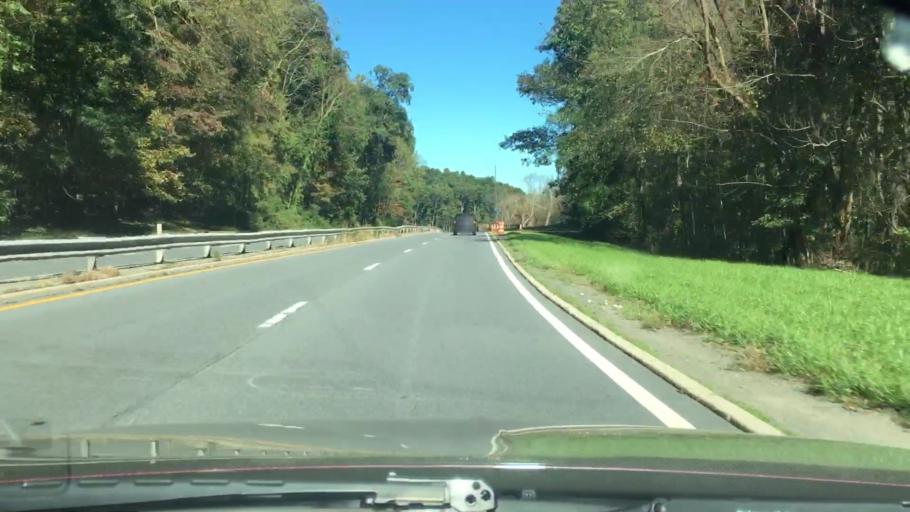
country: US
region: New York
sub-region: Westchester County
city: Mount Kisco
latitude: 41.1988
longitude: -73.7437
